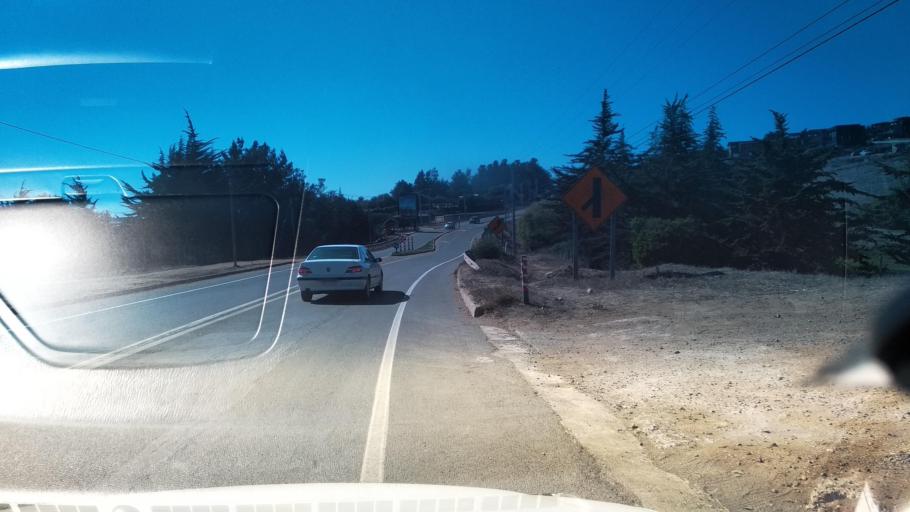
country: CL
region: O'Higgins
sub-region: Provincia de Colchagua
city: Santa Cruz
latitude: -34.4313
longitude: -72.0336
